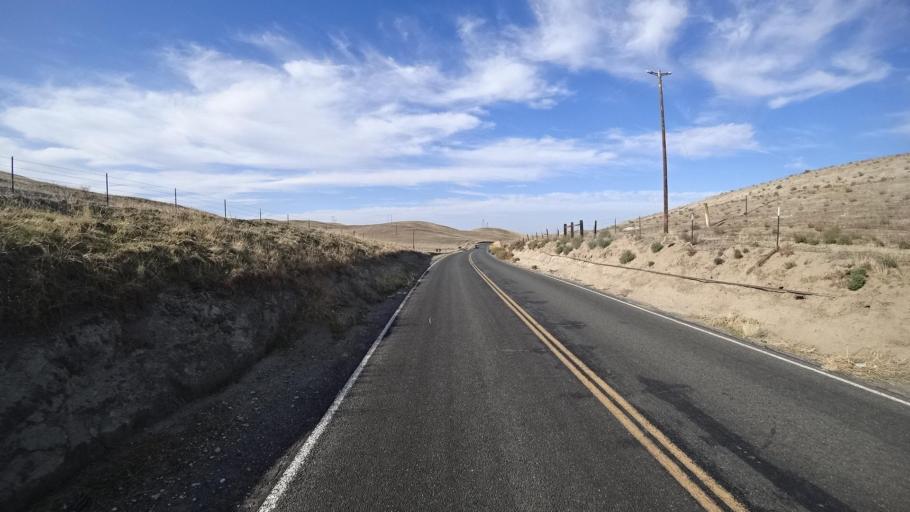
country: US
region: California
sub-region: Kern County
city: Oildale
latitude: 35.6099
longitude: -118.9120
